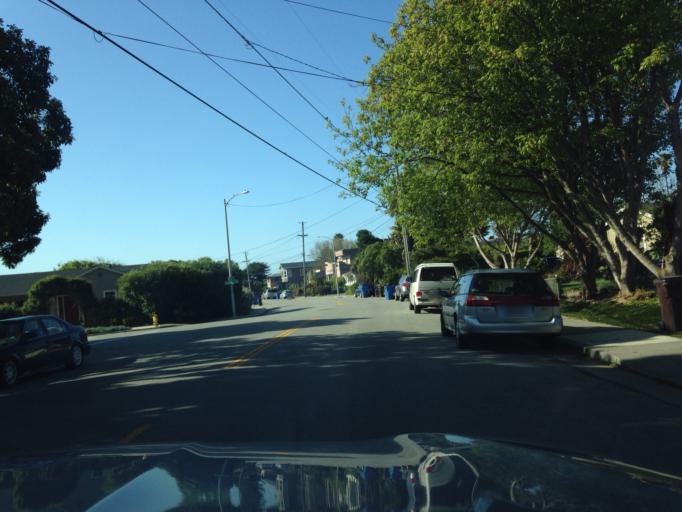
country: US
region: California
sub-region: Santa Cruz County
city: Santa Cruz
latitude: 36.9530
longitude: -122.0446
